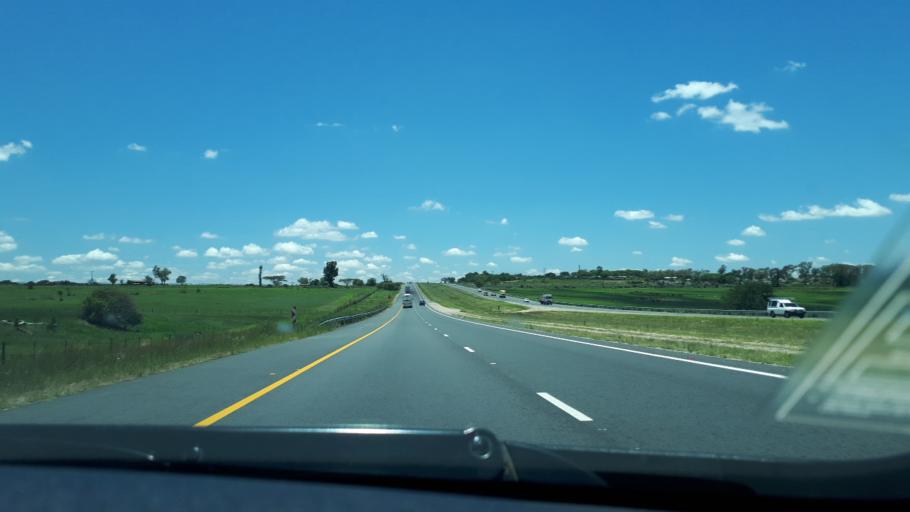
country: ZA
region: Gauteng
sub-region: City of Johannesburg Metropolitan Municipality
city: Diepsloot
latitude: -25.9378
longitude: 27.9743
